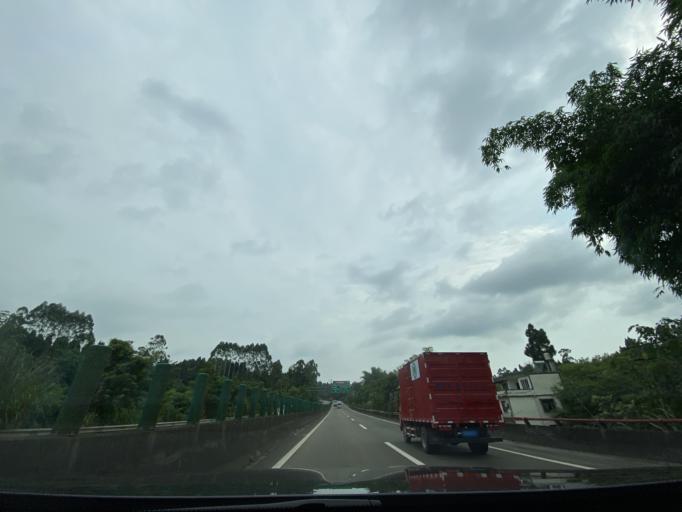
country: CN
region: Sichuan
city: Neijiang
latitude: 29.6377
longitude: 104.9842
